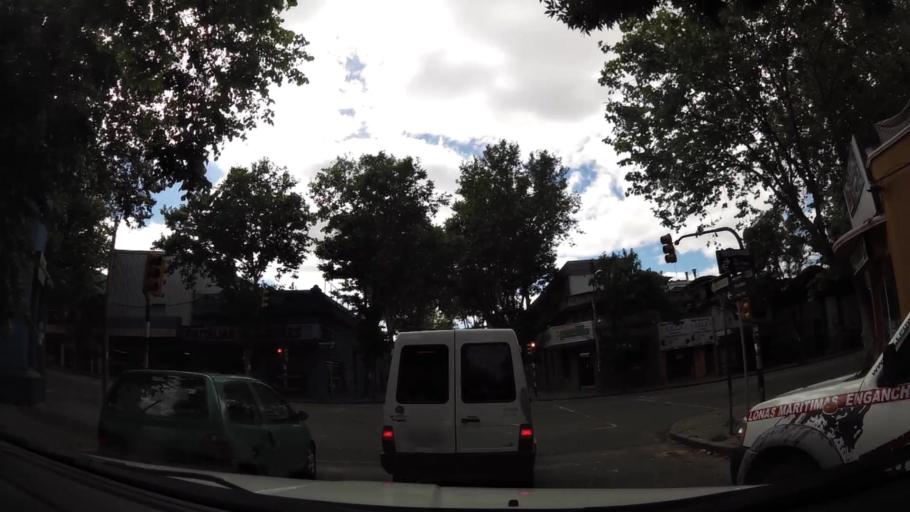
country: UY
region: Montevideo
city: Montevideo
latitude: -34.8782
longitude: -56.1807
